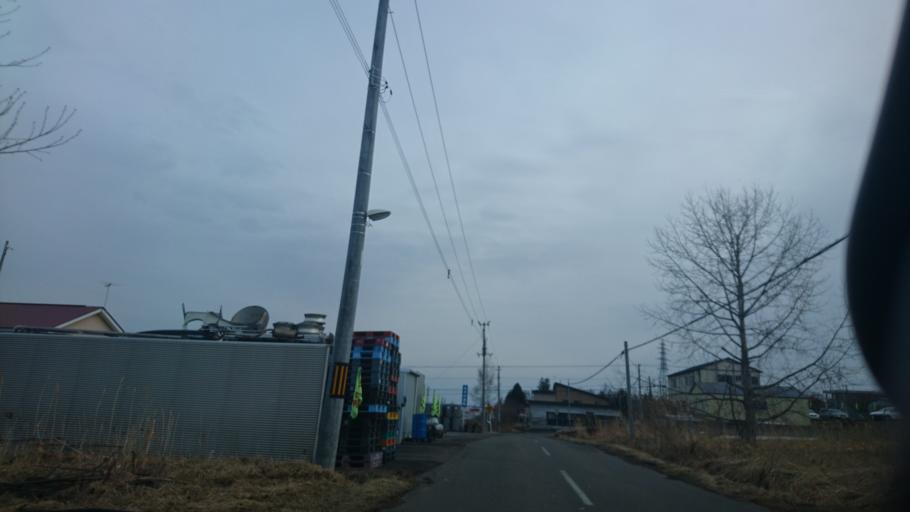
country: JP
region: Hokkaido
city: Otofuke
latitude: 42.9781
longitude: 143.2048
